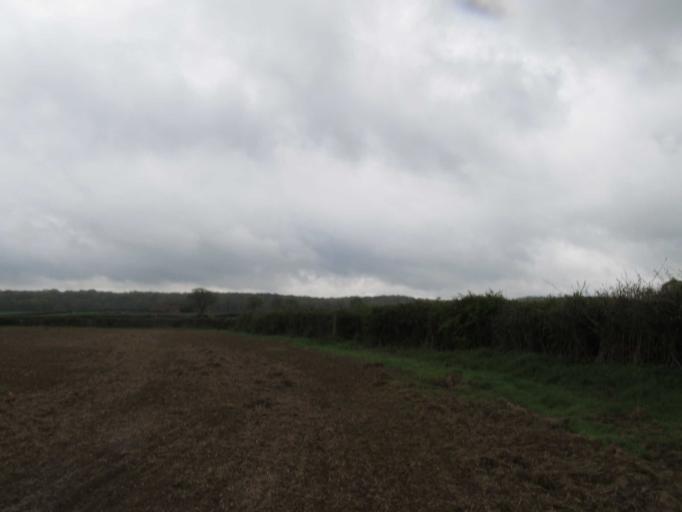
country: GB
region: England
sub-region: Surrey
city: Chiddingfold
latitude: 51.0770
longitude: -0.6388
